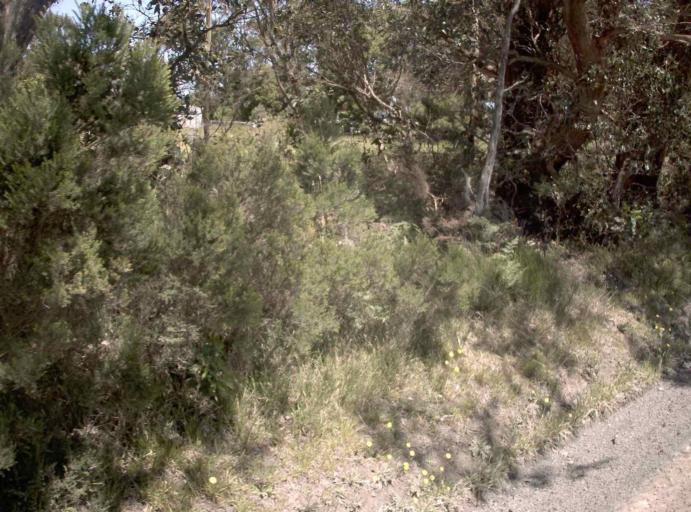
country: AU
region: Victoria
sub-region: Bass Coast
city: North Wonthaggi
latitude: -38.7607
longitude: 146.0689
